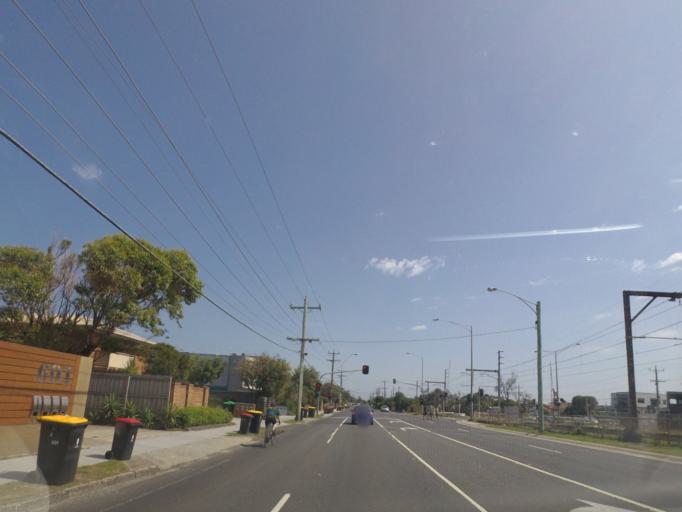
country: AU
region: Victoria
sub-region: Kingston
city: Bonbeach
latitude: -38.0718
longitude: 145.1213
